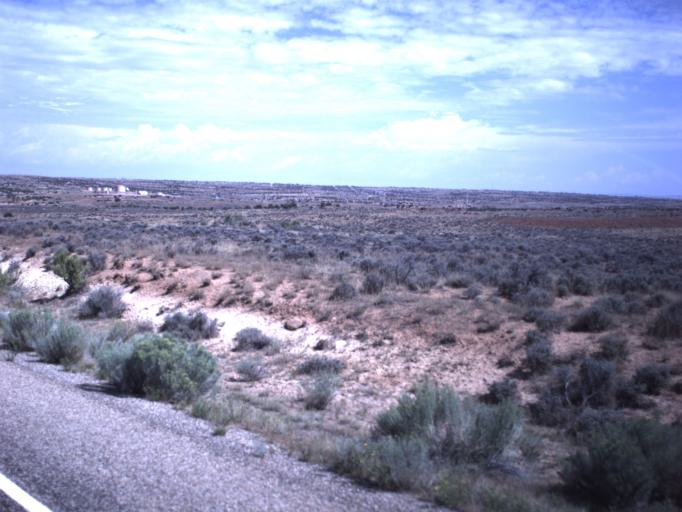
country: US
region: Utah
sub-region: Uintah County
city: Naples
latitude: 40.1571
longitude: -109.3066
